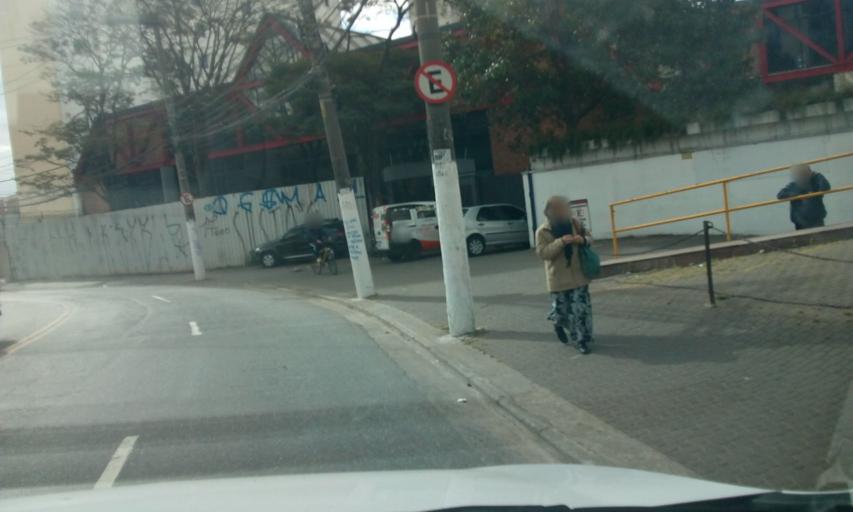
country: BR
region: Sao Paulo
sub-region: Diadema
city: Diadema
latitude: -23.6476
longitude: -46.6624
